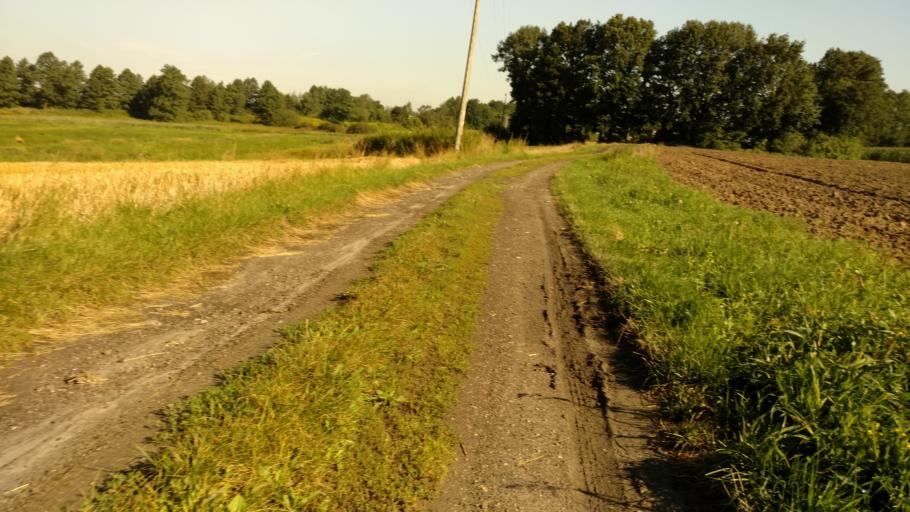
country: PL
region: Silesian Voivodeship
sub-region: Powiat pszczynski
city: Pszczyna
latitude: 49.9798
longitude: 18.9716
